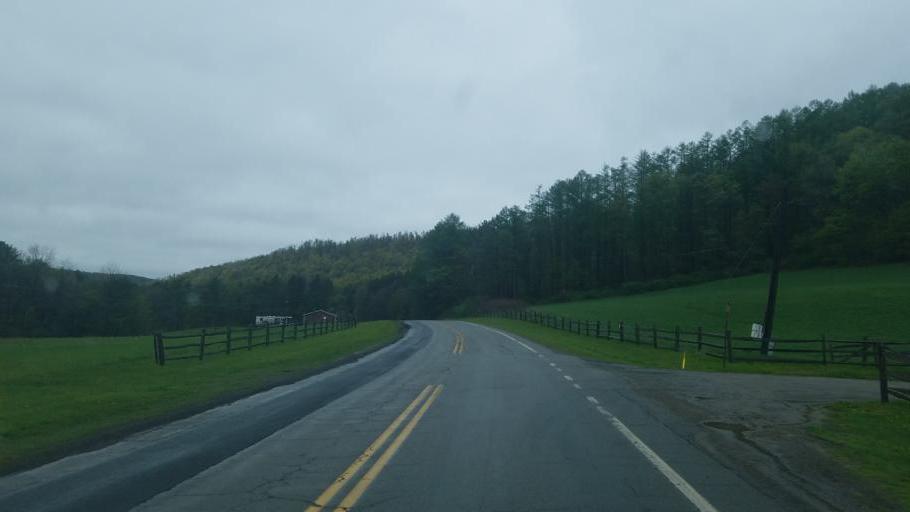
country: US
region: Pennsylvania
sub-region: Potter County
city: Coudersport
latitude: 41.8240
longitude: -77.9718
